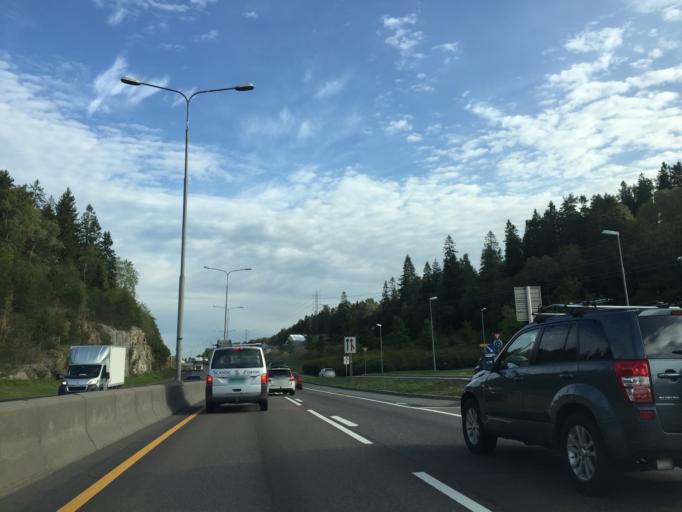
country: NO
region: Akershus
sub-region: Oppegard
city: Kolbotn
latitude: 59.8631
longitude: 10.8308
